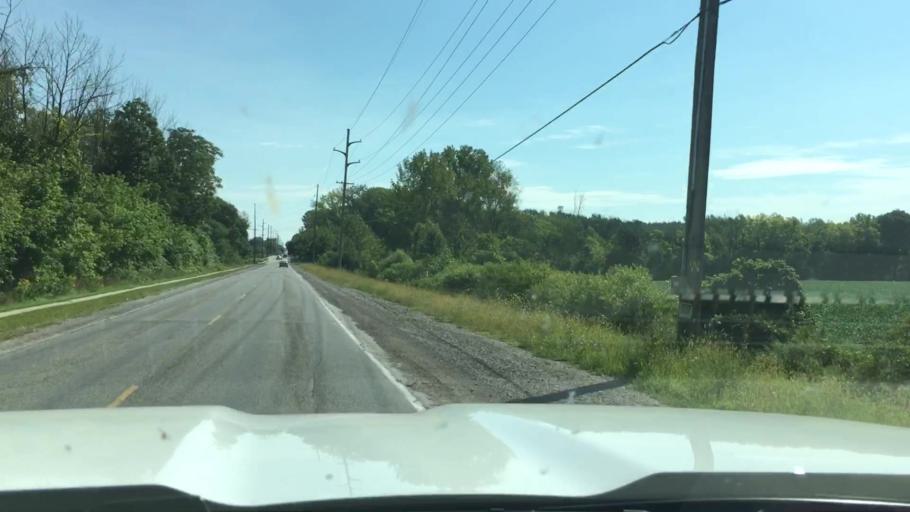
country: US
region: Michigan
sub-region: Saginaw County
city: Freeland
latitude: 43.5250
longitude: -84.1327
